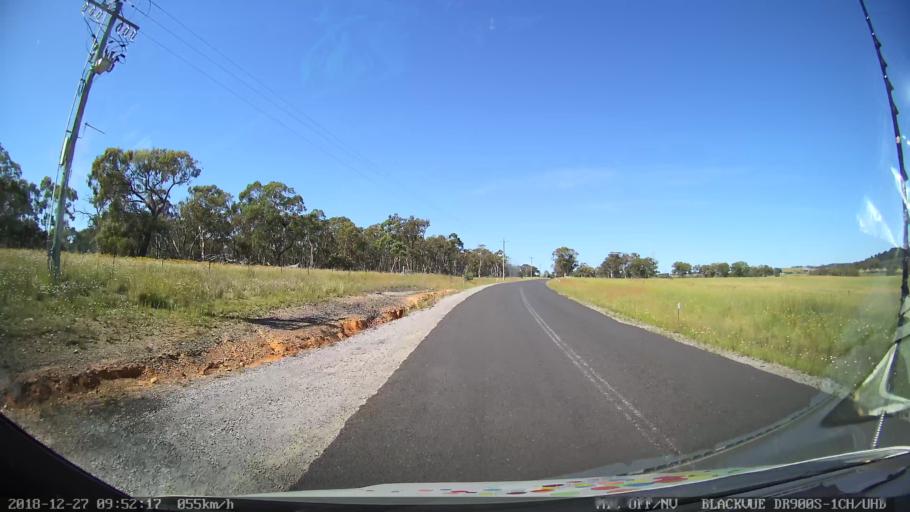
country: AU
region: New South Wales
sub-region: Lithgow
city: Portland
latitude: -33.3719
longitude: 149.9934
